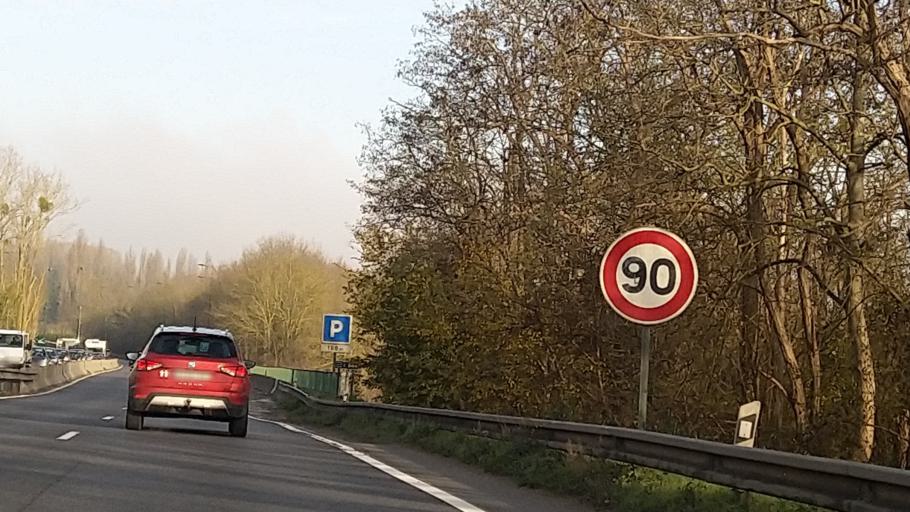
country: FR
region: Ile-de-France
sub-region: Departement du Val-d'Oise
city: Mours
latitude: 49.1303
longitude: 2.2560
